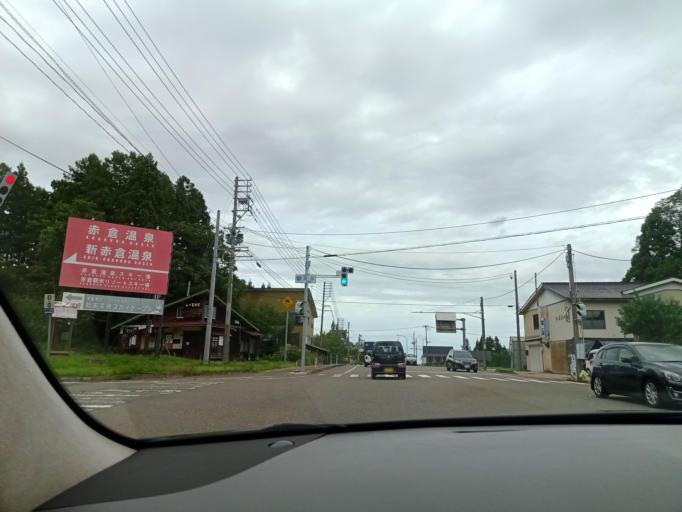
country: JP
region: Niigata
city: Arai
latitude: 36.8863
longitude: 138.2055
